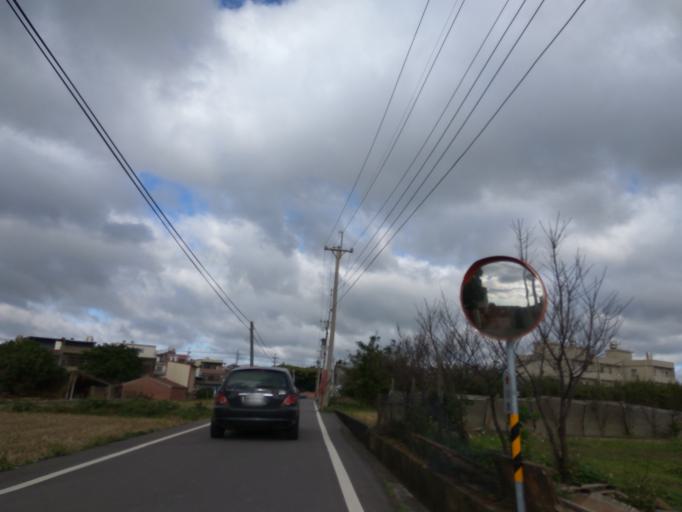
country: TW
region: Taiwan
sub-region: Hsinchu
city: Zhubei
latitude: 24.9751
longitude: 121.0831
